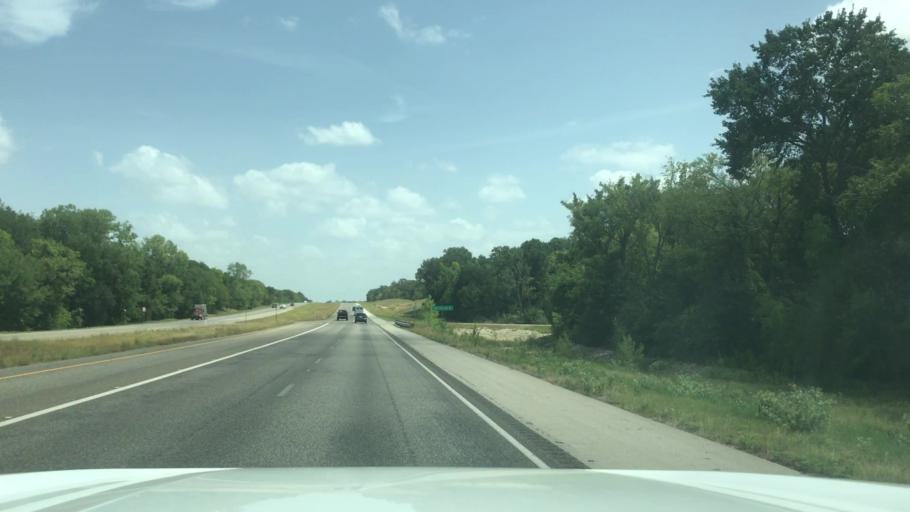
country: US
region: Texas
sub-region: Robertson County
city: Calvert
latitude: 30.9437
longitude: -96.6450
